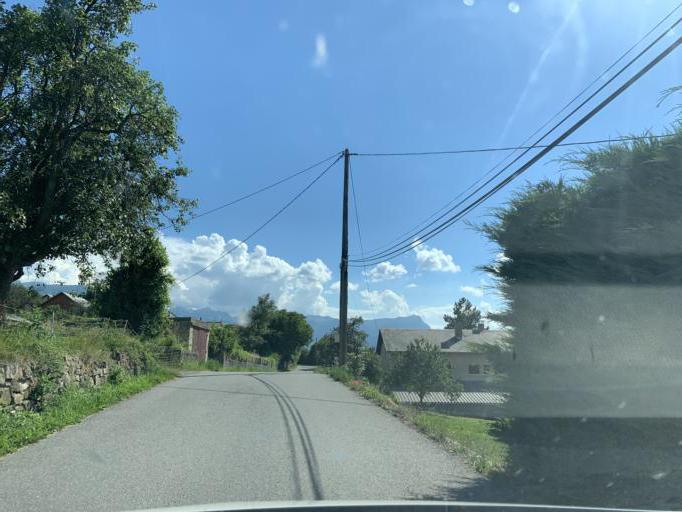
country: FR
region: Provence-Alpes-Cote d'Azur
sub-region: Departement des Hautes-Alpes
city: Embrun
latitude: 44.5840
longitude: 6.5299
